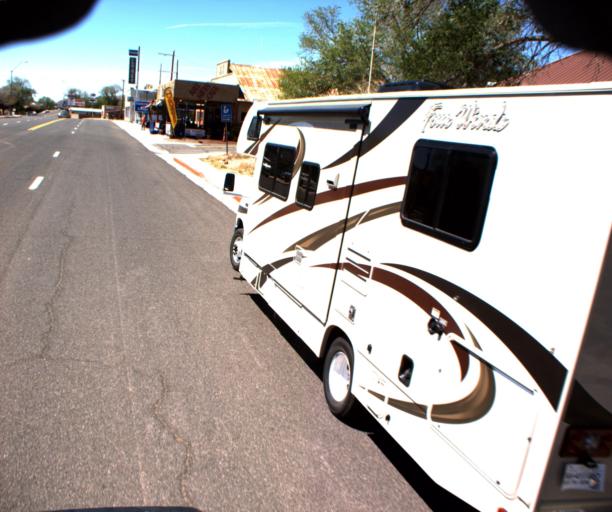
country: US
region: Arizona
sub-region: Mohave County
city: Peach Springs
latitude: 35.3264
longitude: -112.8737
